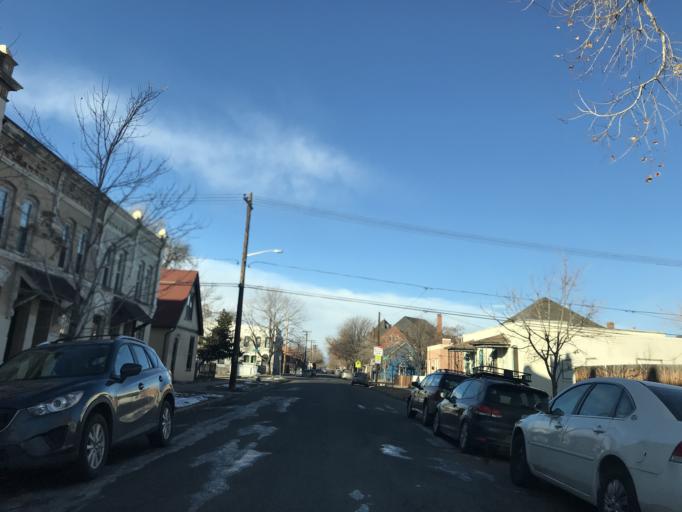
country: US
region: Colorado
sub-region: Denver County
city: Denver
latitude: 39.7670
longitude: -104.9649
